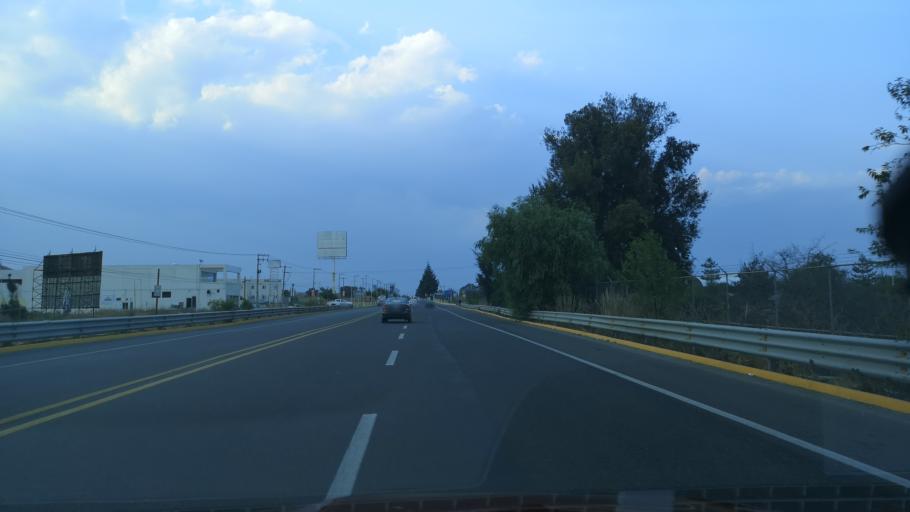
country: MX
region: Puebla
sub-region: Huejotzingo
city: Los Encinos
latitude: 19.1594
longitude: -98.3772
